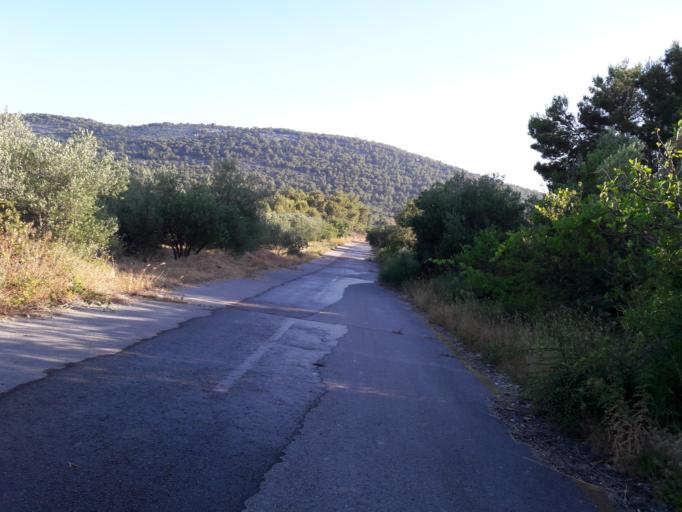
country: HR
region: Sibensko-Kniniska
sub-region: Grad Sibenik
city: Sibenik
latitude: 43.6967
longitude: 15.8467
